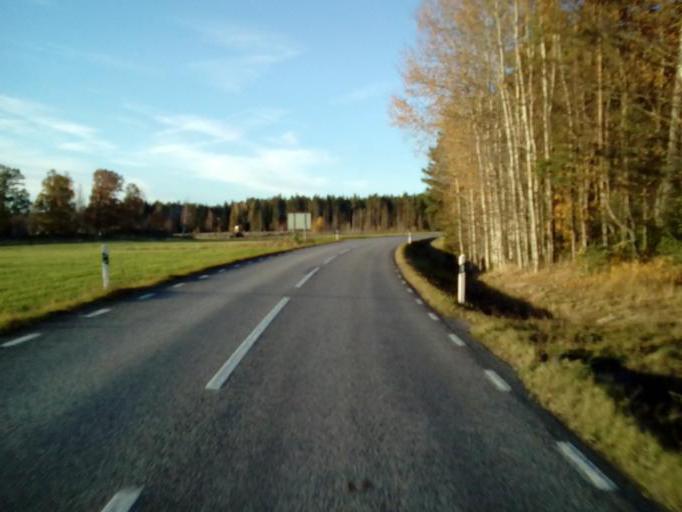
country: SE
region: OErebro
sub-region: Hallsbergs Kommun
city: Palsboda
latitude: 59.0276
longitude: 15.3662
